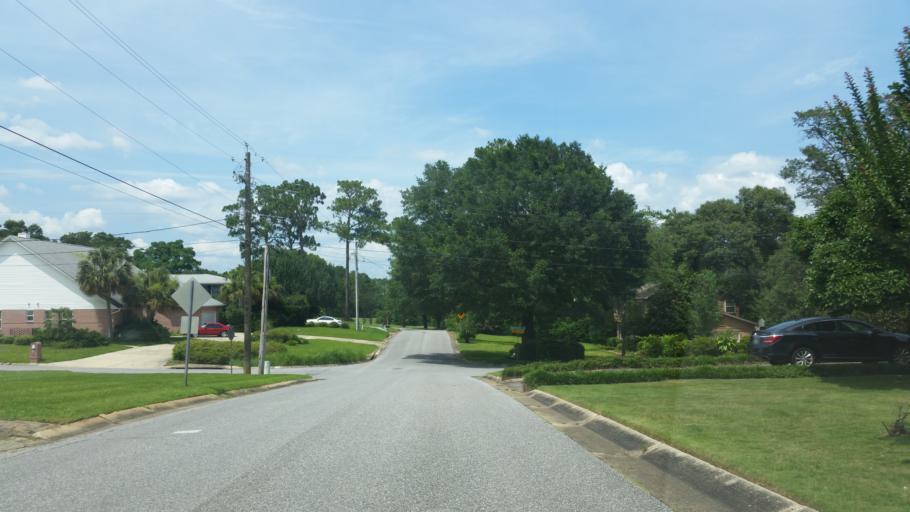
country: US
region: Florida
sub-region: Escambia County
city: Ferry Pass
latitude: 30.5401
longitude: -87.2323
